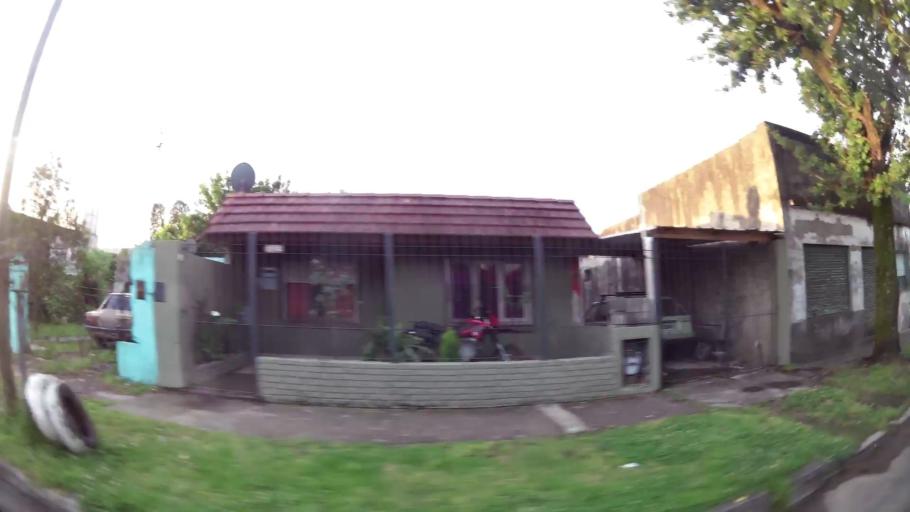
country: AR
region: Buenos Aires
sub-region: Partido de Almirante Brown
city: Adrogue
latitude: -34.7638
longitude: -58.3549
